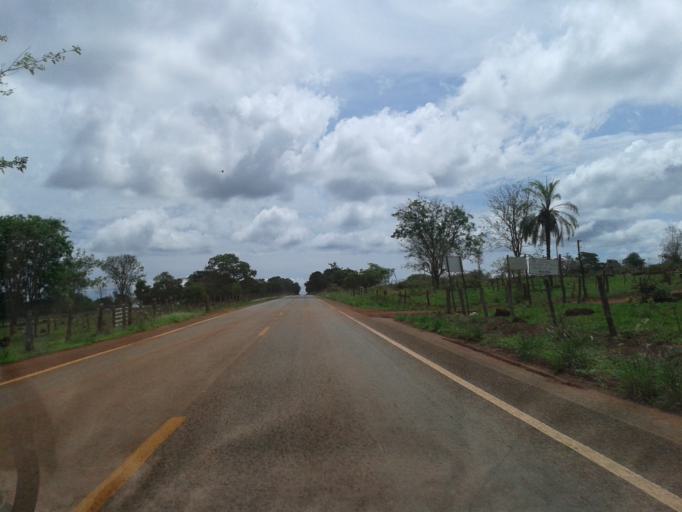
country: BR
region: Goias
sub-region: Buriti Alegre
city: Buriti Alegre
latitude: -18.1259
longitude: -49.1339
